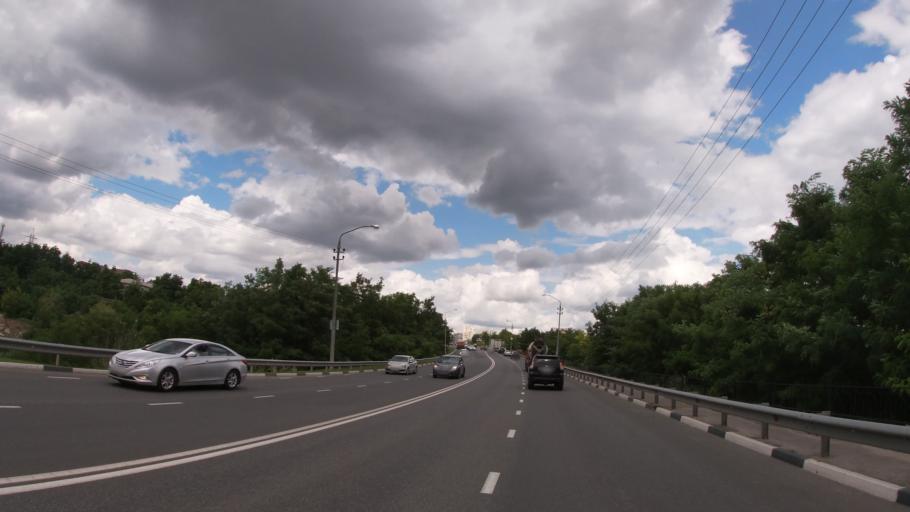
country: RU
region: Belgorod
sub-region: Belgorodskiy Rayon
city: Belgorod
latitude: 50.5590
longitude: 36.5864
